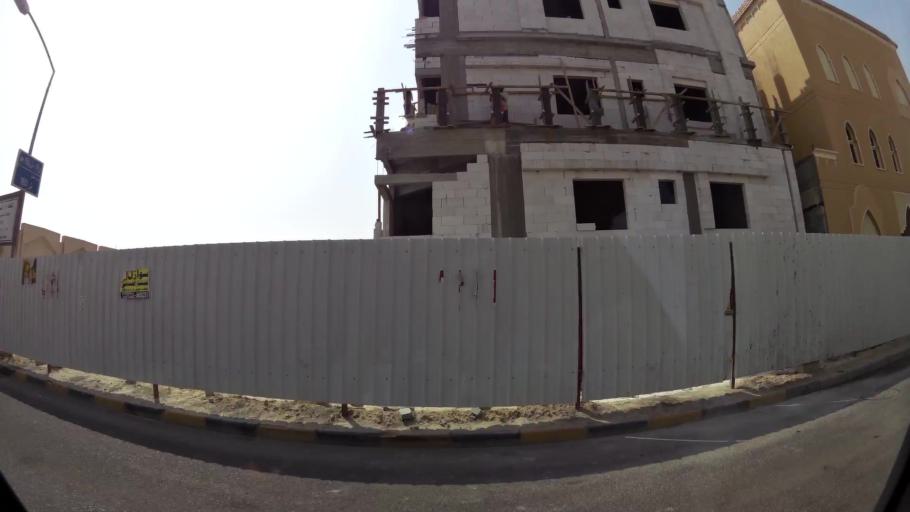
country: KW
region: Muhafazat al Jahra'
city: Al Jahra'
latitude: 29.3248
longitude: 47.7404
